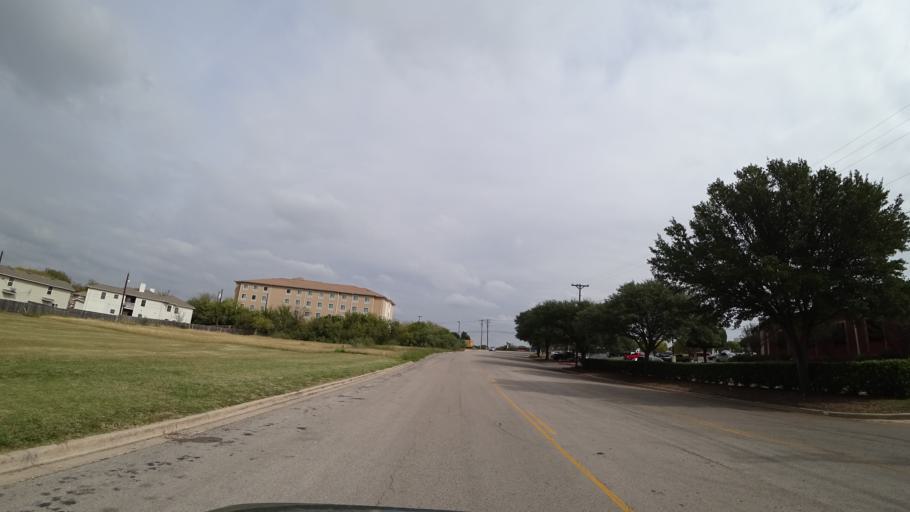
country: US
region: Texas
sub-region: Williamson County
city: Round Rock
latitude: 30.4911
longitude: -97.6797
